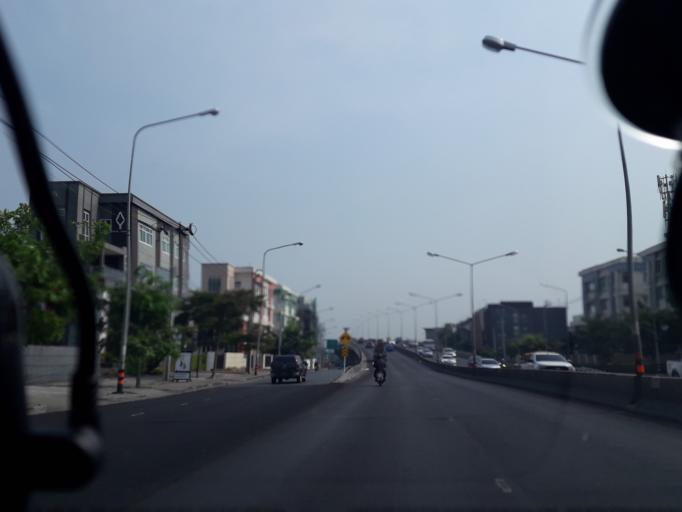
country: TH
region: Bangkok
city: Khan Na Yao
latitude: 13.8186
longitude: 100.6509
